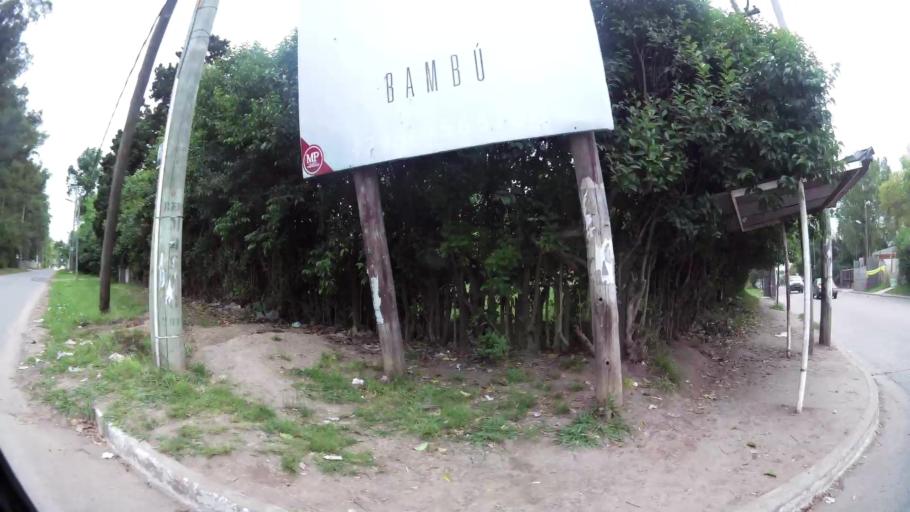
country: AR
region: Buenos Aires
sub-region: Partido de Ezeiza
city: Ezeiza
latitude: -34.8687
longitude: -58.5061
